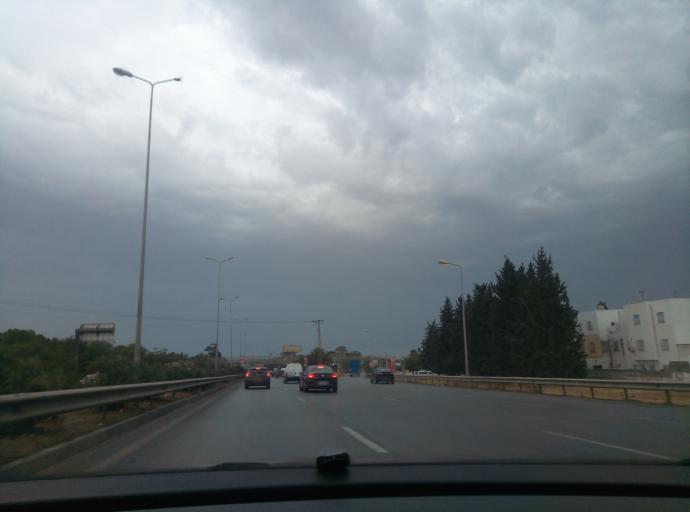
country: TN
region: Bin 'Arus
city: Ben Arous
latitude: 36.7438
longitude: 10.2123
